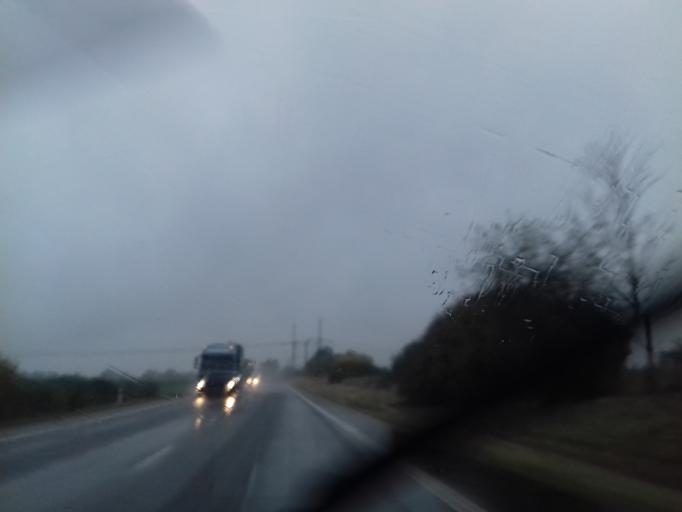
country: CZ
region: Pardubicky
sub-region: Okres Svitavy
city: Moravska Trebova
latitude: 49.7712
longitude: 16.7191
